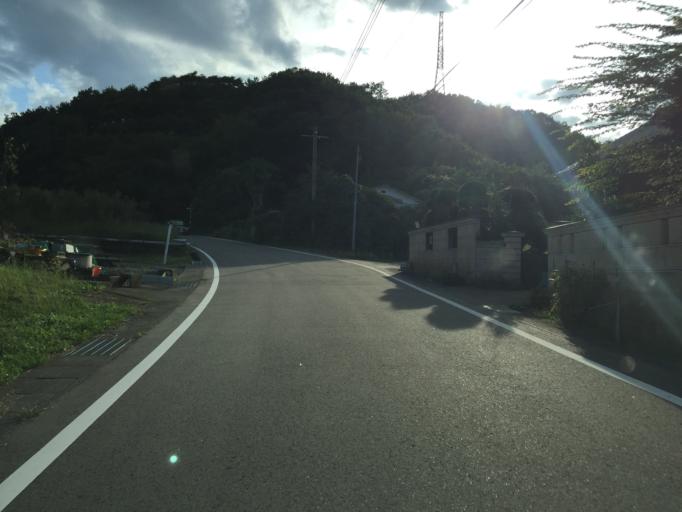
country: JP
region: Fukushima
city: Hobaramachi
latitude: 37.8058
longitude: 140.5416
